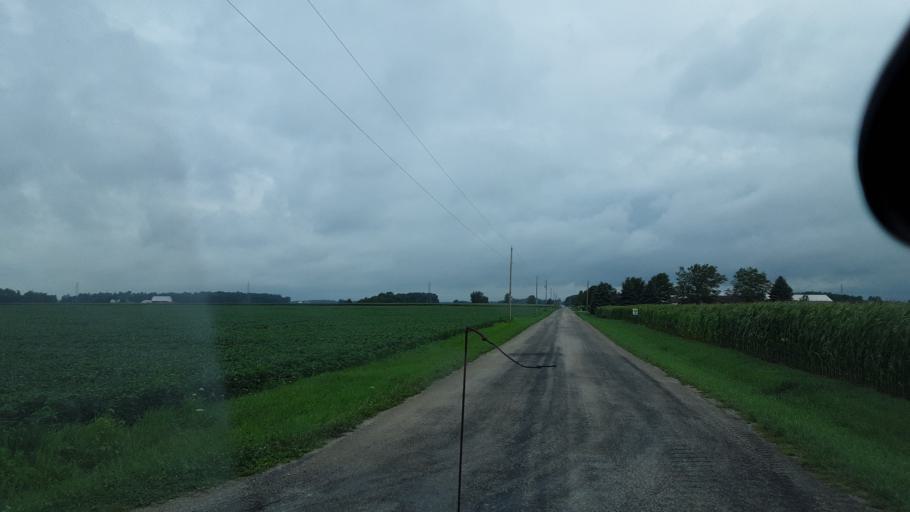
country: US
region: Indiana
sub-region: Allen County
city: Monroeville
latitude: 40.9135
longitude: -84.8427
